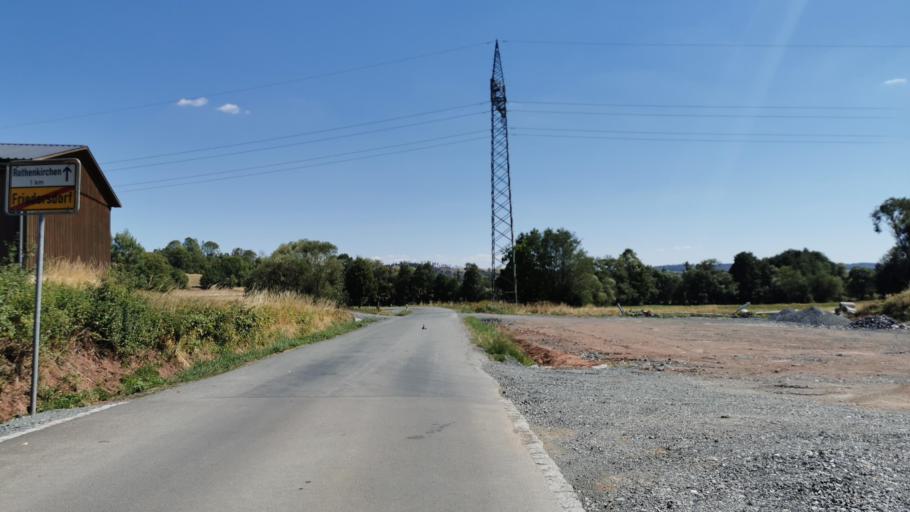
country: DE
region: Bavaria
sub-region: Upper Franconia
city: Pressig
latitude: 50.3698
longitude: 11.3035
